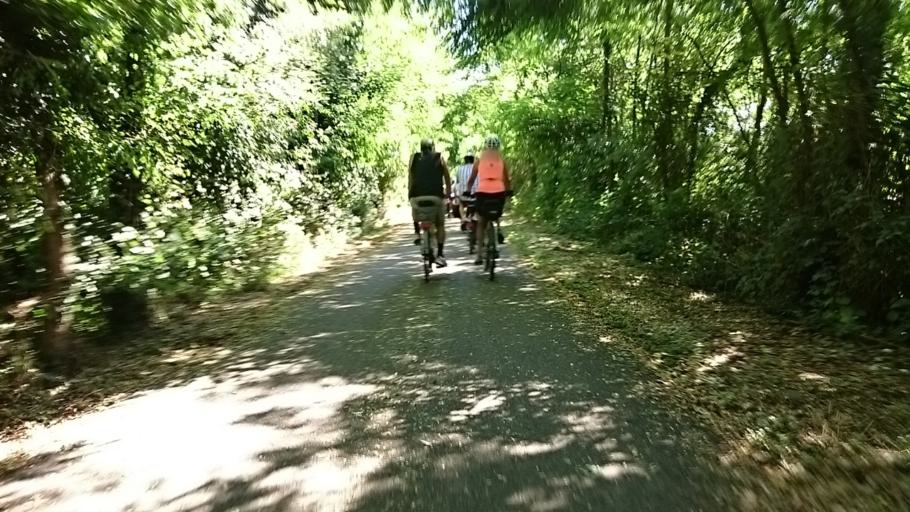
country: IT
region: Veneto
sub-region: Provincia di Padova
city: Piombino Dese
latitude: 45.6038
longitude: 12.0107
